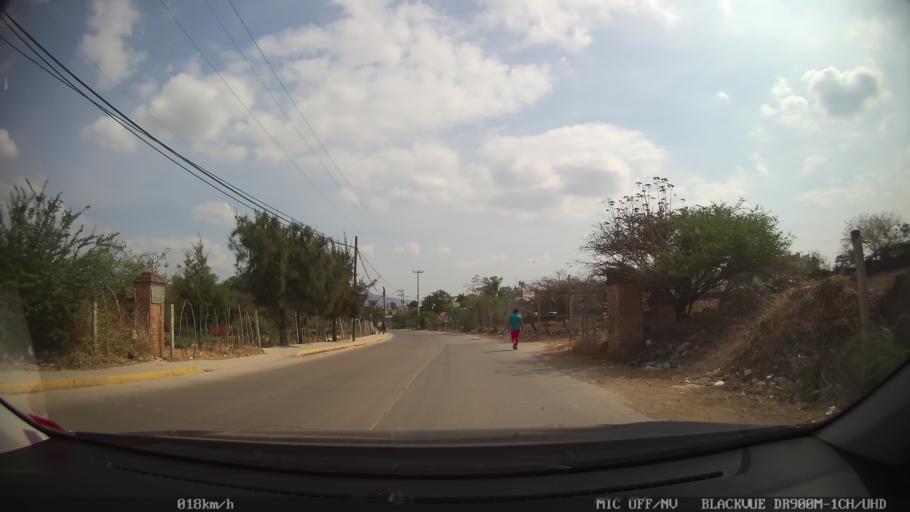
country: MX
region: Jalisco
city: Coyula
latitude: 20.6485
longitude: -103.2140
